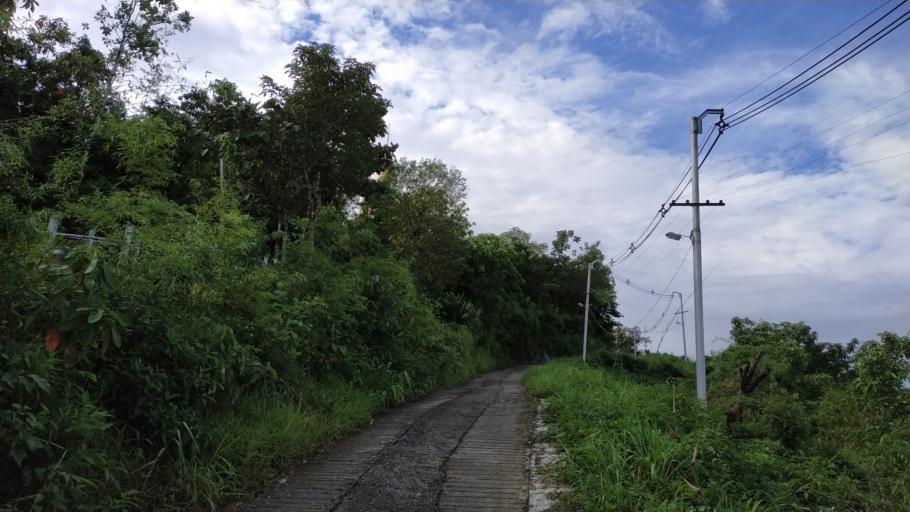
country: MM
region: Mon
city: Thaton
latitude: 16.9264
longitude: 97.3818
